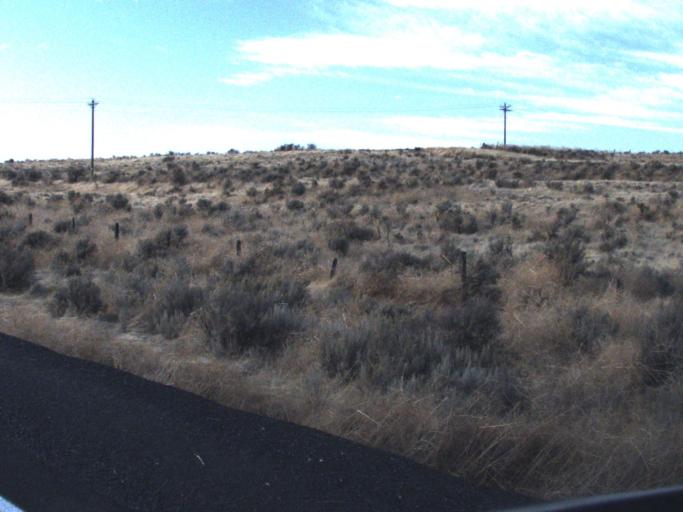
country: US
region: Washington
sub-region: Grant County
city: Warden
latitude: 47.3182
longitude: -118.8503
